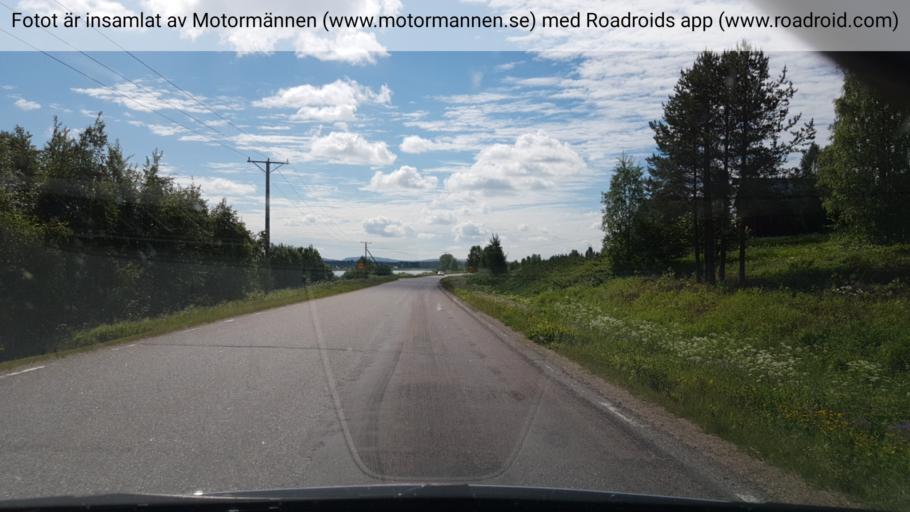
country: FI
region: Lapland
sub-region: Torniolaakso
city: Pello
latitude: 66.6530
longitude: 23.8599
